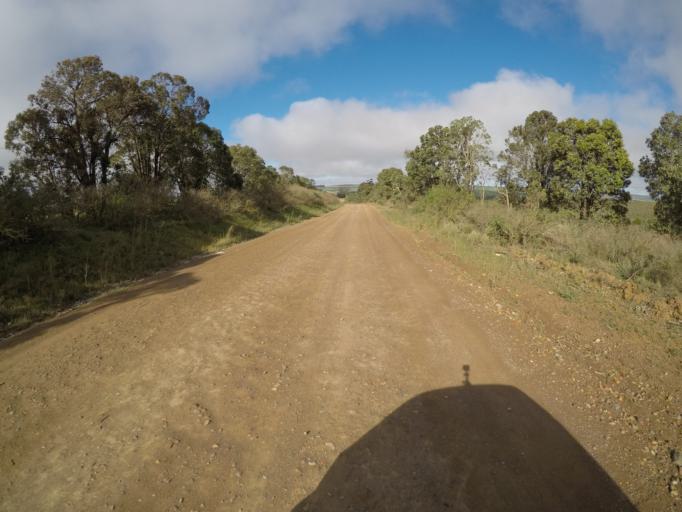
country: ZA
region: Western Cape
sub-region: Cape Winelands District Municipality
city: Ashton
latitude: -34.1178
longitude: 19.8053
